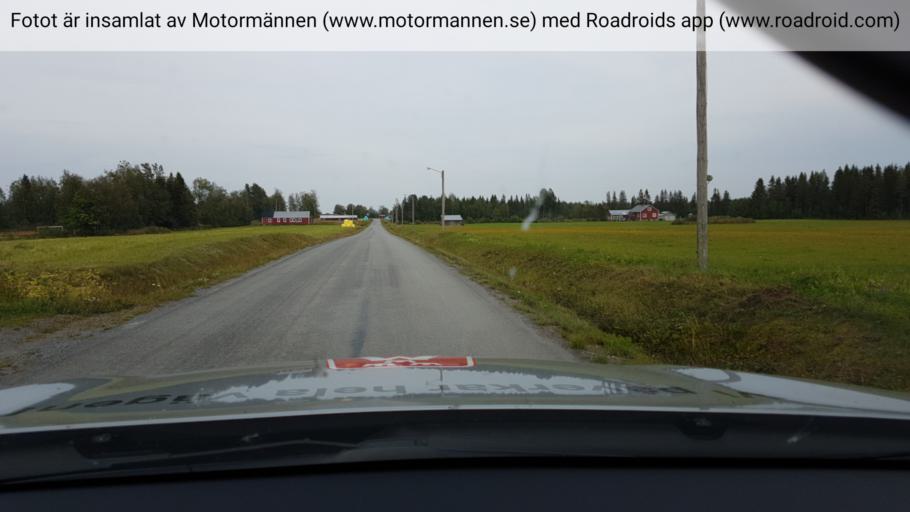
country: SE
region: Jaemtland
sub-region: OEstersunds Kommun
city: Lit
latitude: 63.6794
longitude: 14.8319
